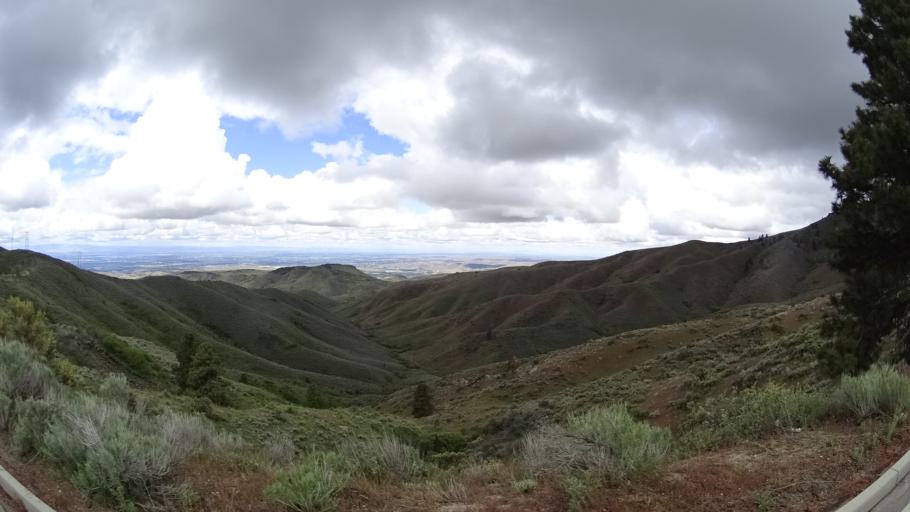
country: US
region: Idaho
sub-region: Ada County
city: Boise
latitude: 43.7250
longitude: -116.1576
